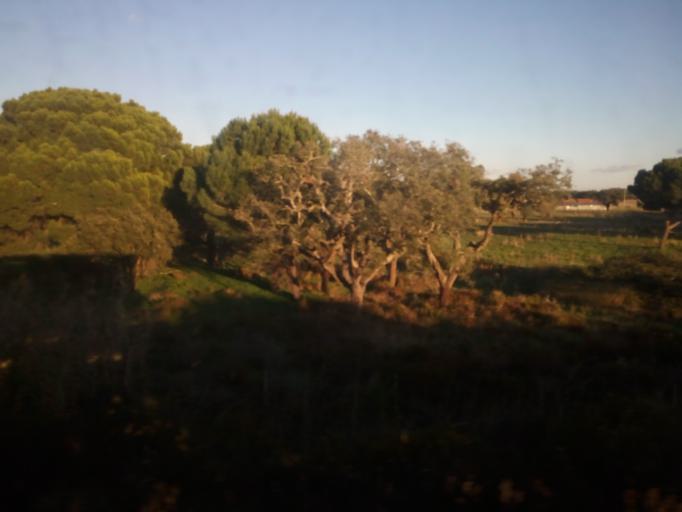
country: PT
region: Setubal
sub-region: Grandola
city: Grandola
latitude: 38.1862
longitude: -8.5555
